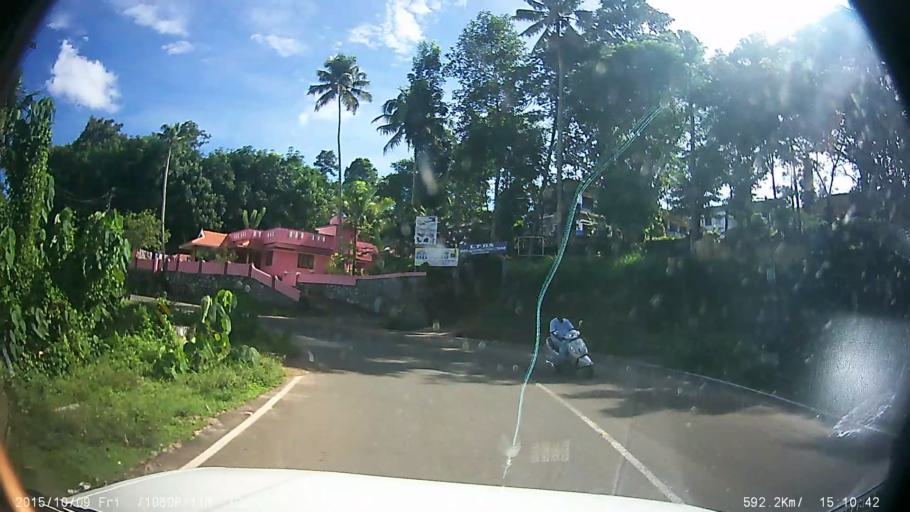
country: IN
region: Kerala
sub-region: Ernakulam
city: Piravam
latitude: 9.8785
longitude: 76.5760
